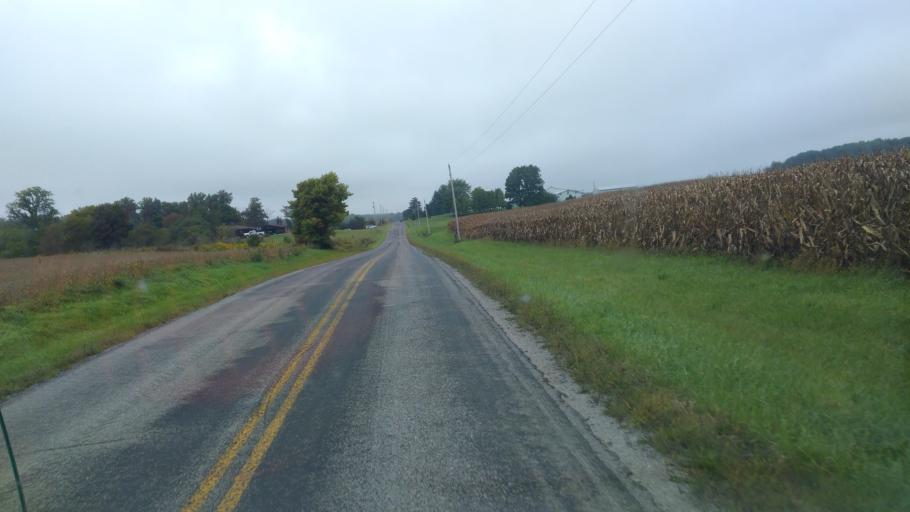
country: US
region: Ohio
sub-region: Hardin County
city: Kenton
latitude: 40.5570
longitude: -83.6360
